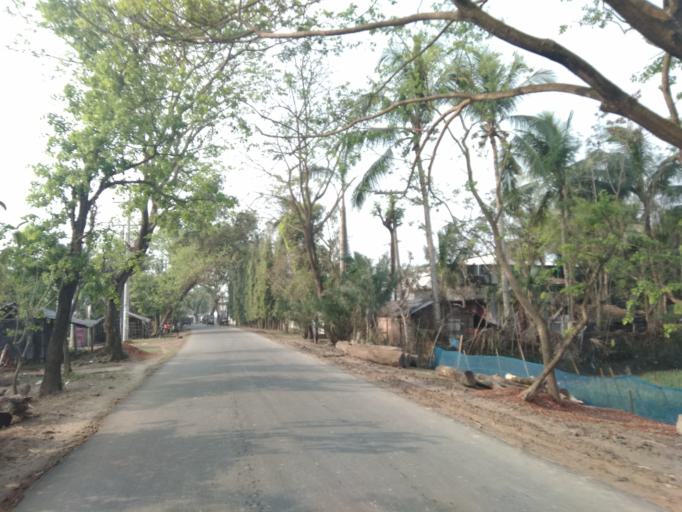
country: IN
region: West Bengal
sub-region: North 24 Parganas
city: Taki
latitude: 22.3280
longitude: 89.1055
